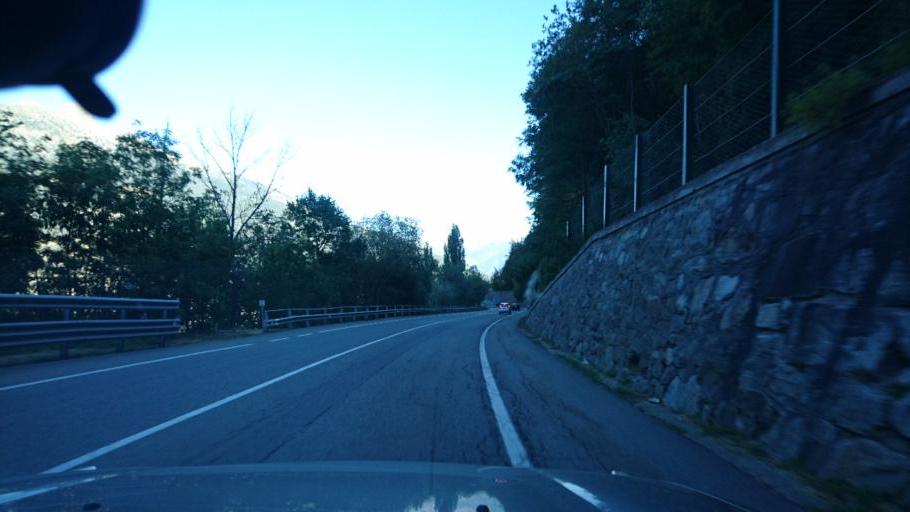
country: IT
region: Aosta Valley
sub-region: Valle d'Aosta
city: Allein
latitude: 45.7979
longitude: 7.2786
